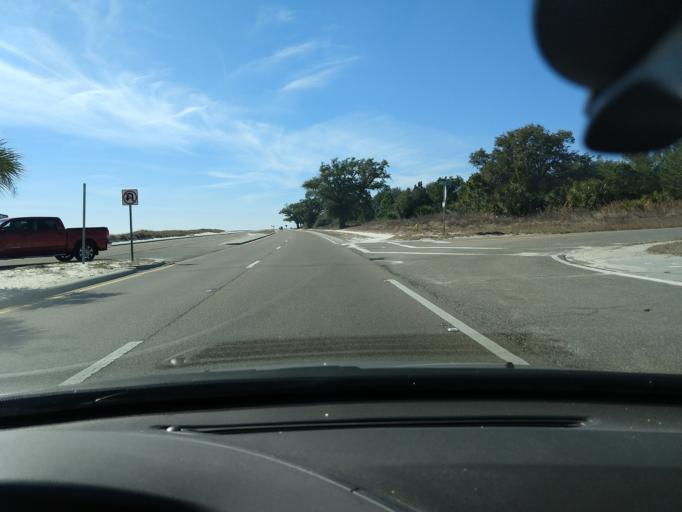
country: US
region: Mississippi
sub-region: Harrison County
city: Long Beach
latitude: 30.3352
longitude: -89.1770
